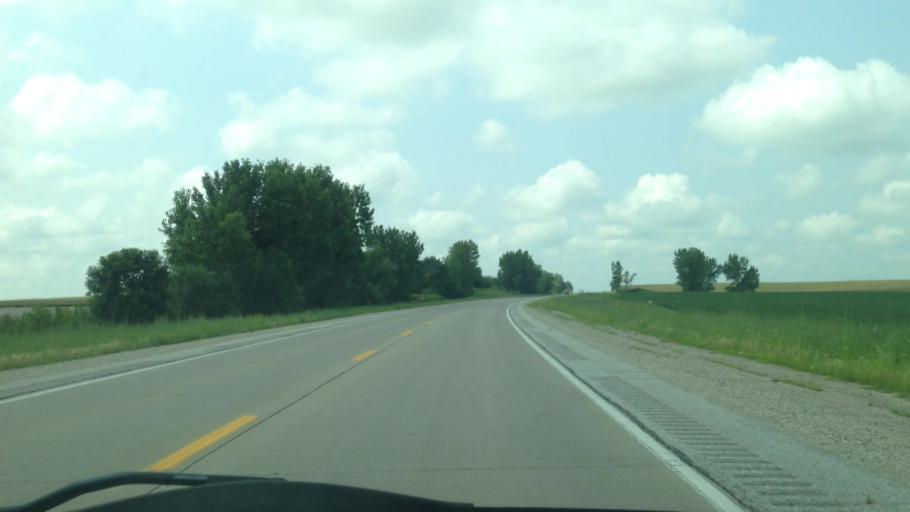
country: US
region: Iowa
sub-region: Linn County
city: Fairfax
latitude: 41.9040
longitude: -91.7990
